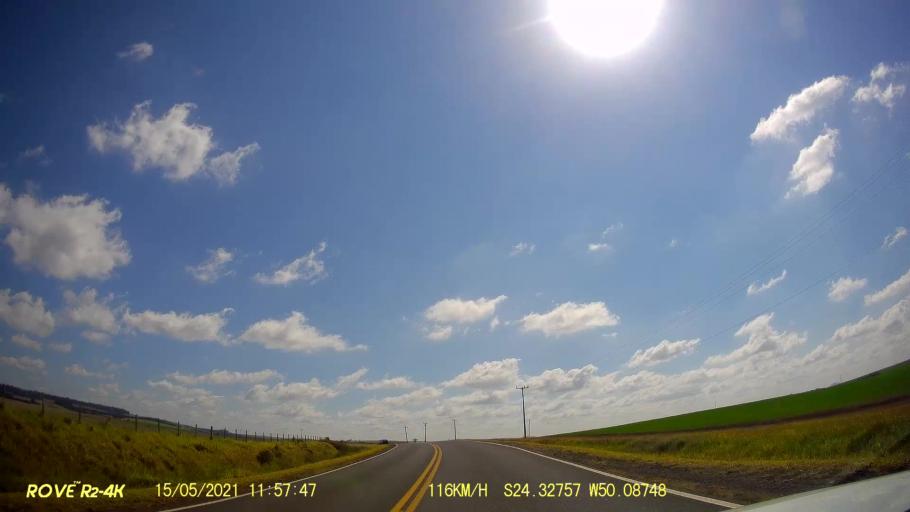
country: BR
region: Parana
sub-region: Pirai Do Sul
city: Pirai do Sul
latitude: -24.3260
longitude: -50.0892
